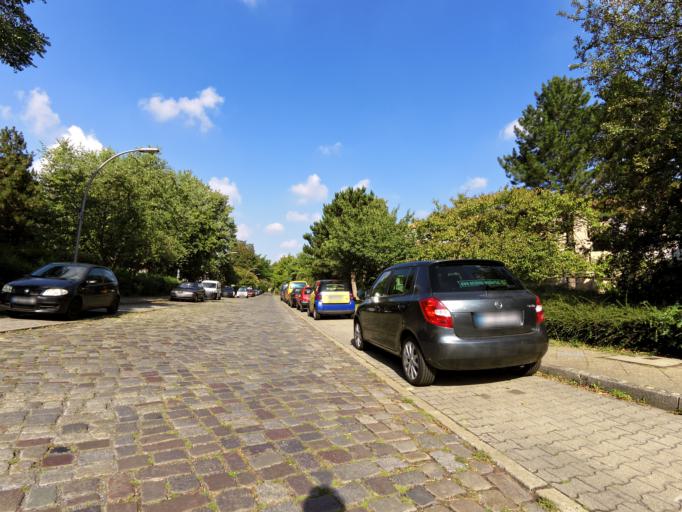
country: DE
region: Berlin
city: Lichtenrade
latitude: 52.3893
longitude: 13.4145
